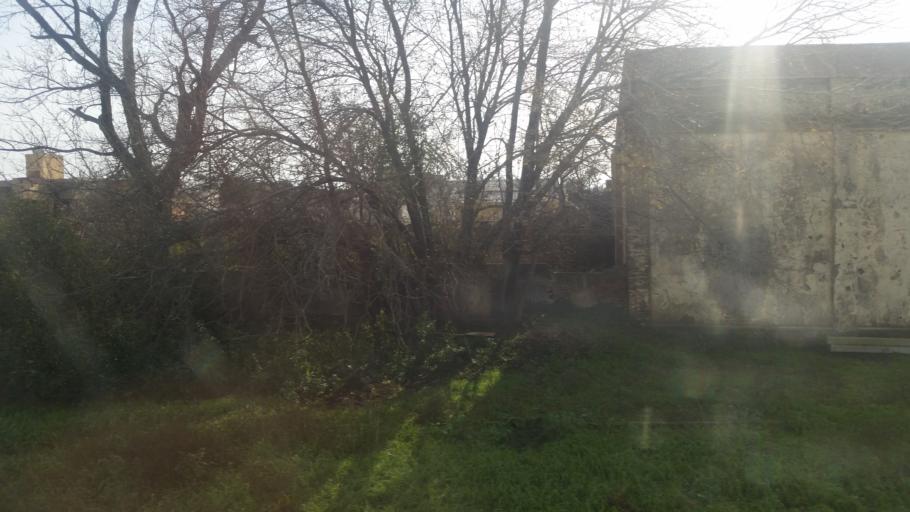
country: AR
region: Cordoba
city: Morrison
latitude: -32.5941
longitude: -62.8383
